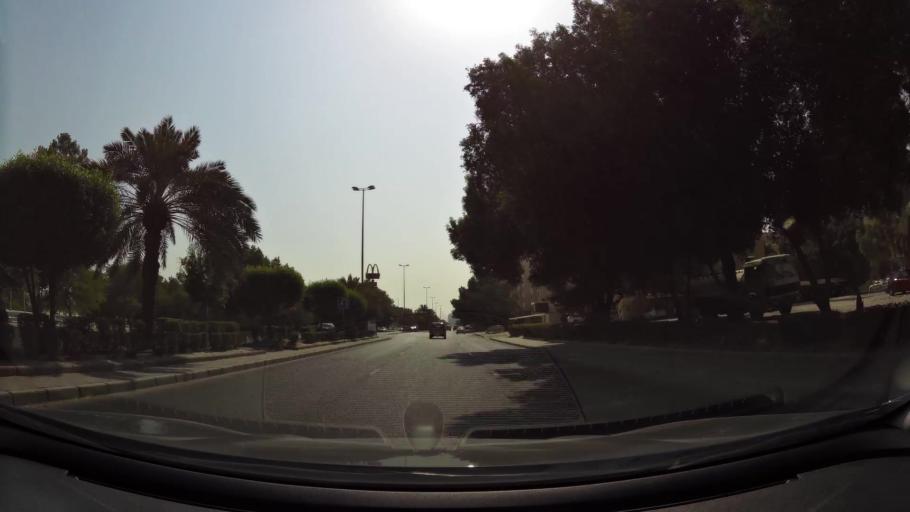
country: KW
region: Al Ahmadi
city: Al Mahbulah
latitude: 29.1453
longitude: 48.1284
